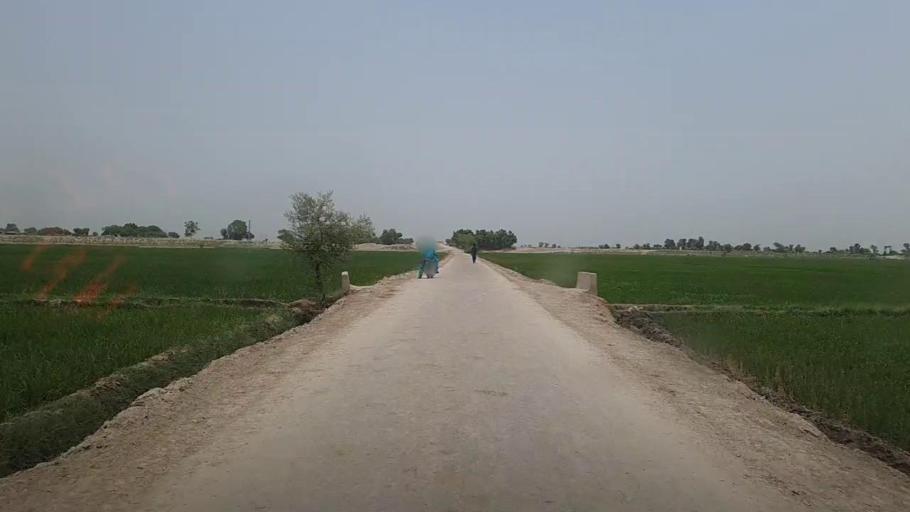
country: PK
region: Sindh
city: Sita Road
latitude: 27.0474
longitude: 67.8471
